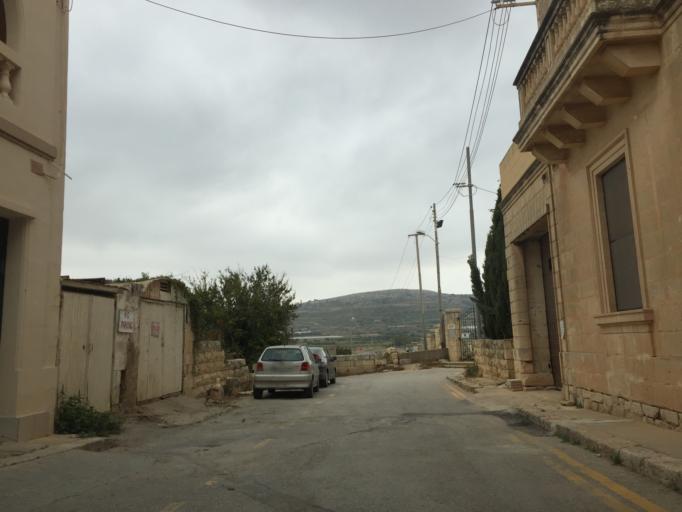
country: MT
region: L-Imgarr
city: Imgarr
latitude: 35.9190
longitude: 14.3687
